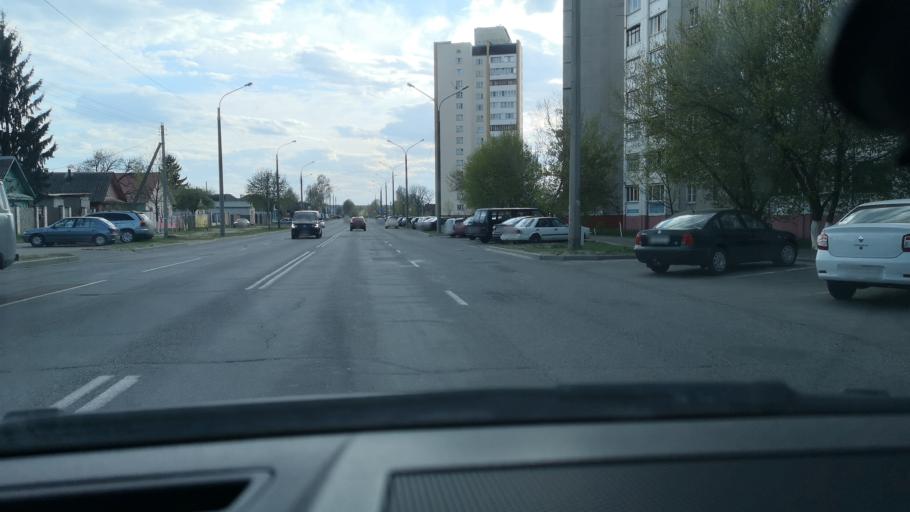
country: BY
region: Gomel
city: Gomel
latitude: 52.4007
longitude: 30.9261
